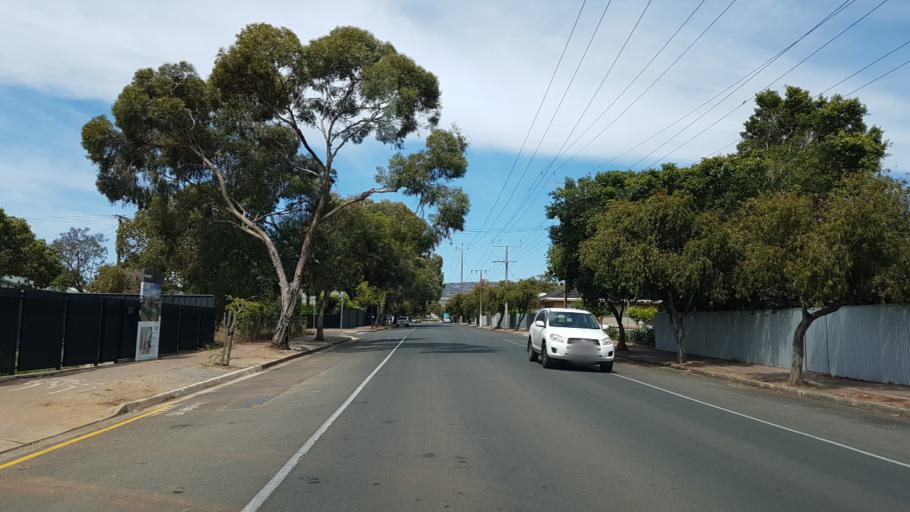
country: AU
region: South Australia
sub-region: Norwood Payneham St Peters
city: Trinity Gardens
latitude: -34.9120
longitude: 138.6432
